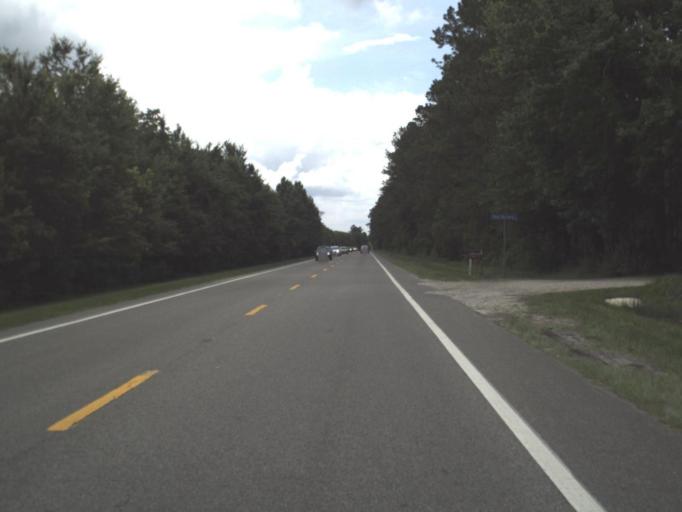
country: US
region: Florida
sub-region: Nassau County
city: Yulee
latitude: 30.6551
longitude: -81.6279
